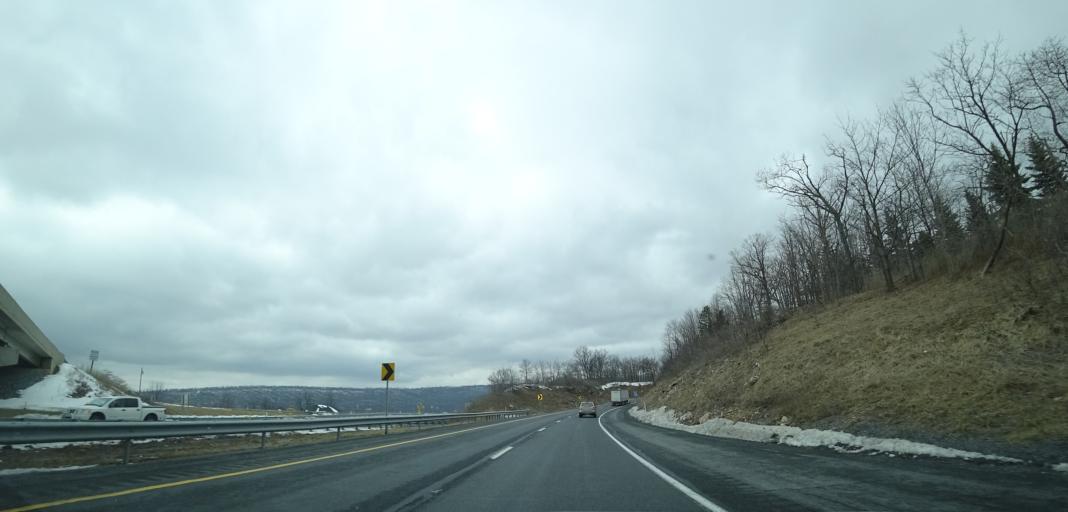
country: US
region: Pennsylvania
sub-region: Bedford County
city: Earlston
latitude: 39.8855
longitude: -78.2439
